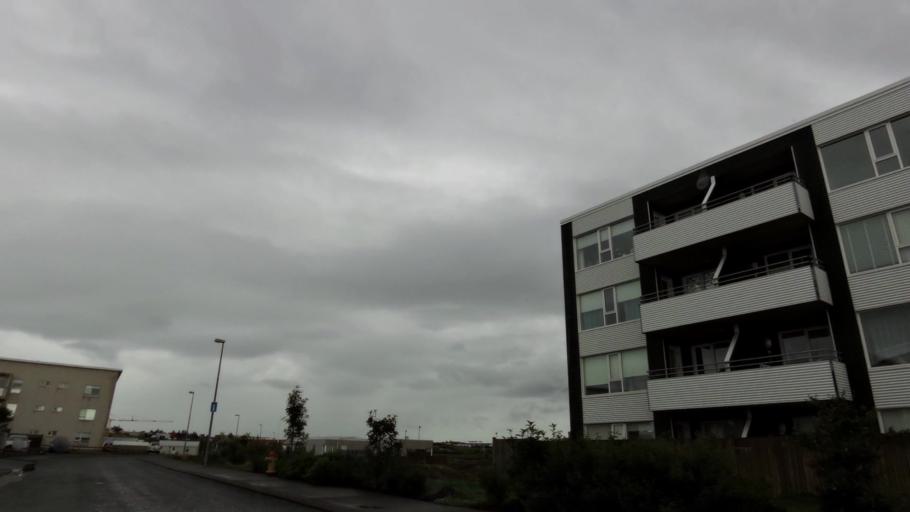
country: IS
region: Capital Region
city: Hafnarfjoerdur
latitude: 64.0495
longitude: -21.9756
